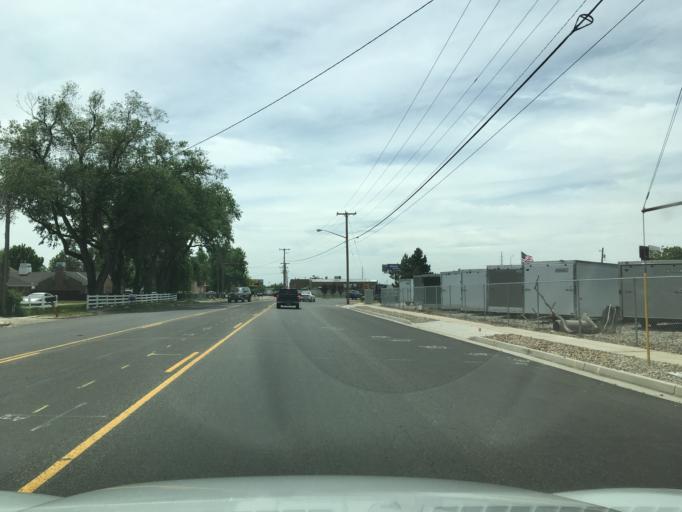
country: US
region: Utah
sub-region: Davis County
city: Layton
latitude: 41.0526
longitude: -111.9578
